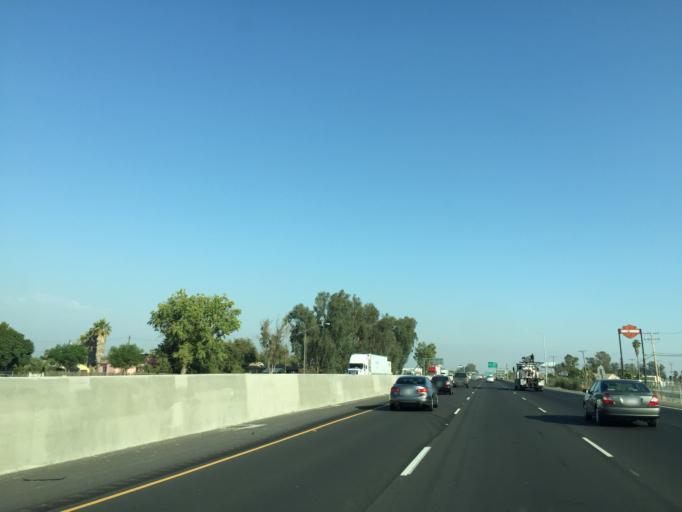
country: US
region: California
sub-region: Tulare County
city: Goshen
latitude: 36.3483
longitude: -119.4255
